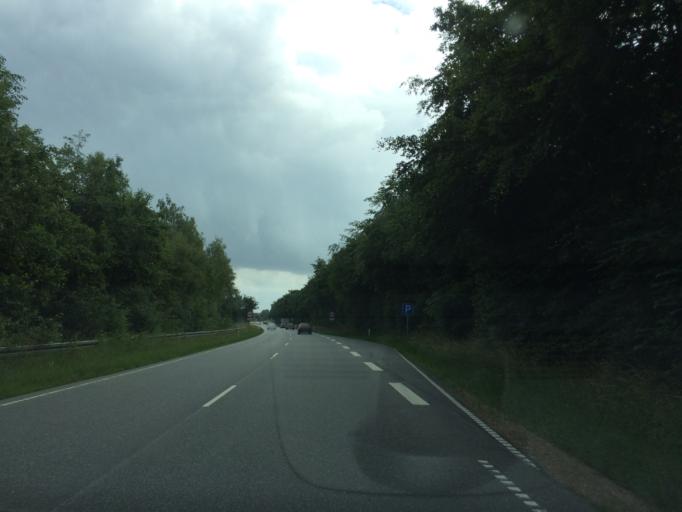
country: DK
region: Zealand
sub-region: Odsherred Kommune
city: Hojby
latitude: 55.9261
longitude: 11.5417
